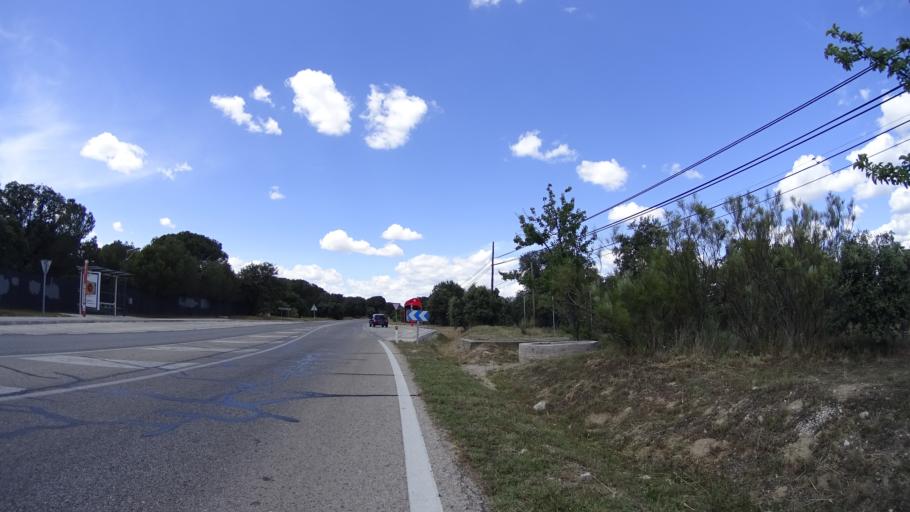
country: ES
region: Madrid
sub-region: Provincia de Madrid
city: Boadilla del Monte
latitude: 40.4295
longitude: -3.8698
